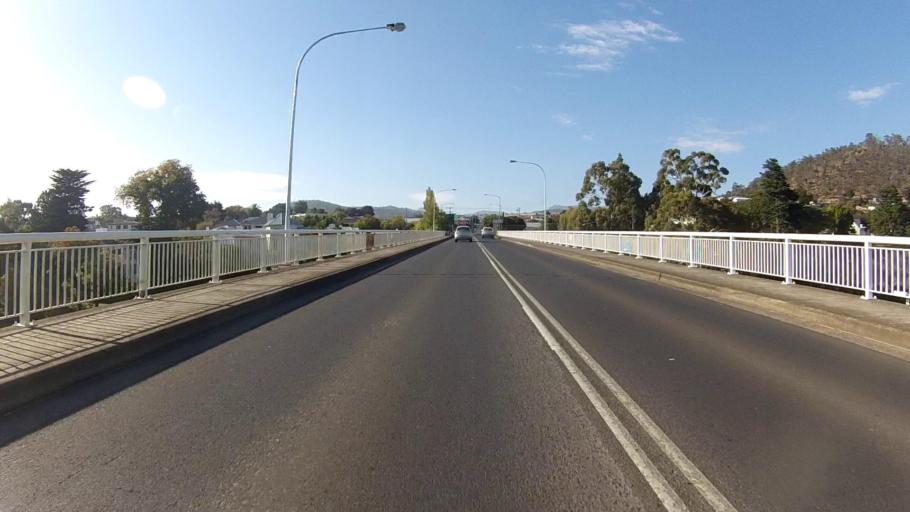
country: AU
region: Tasmania
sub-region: Derwent Valley
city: New Norfolk
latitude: -42.7788
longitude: 147.0564
